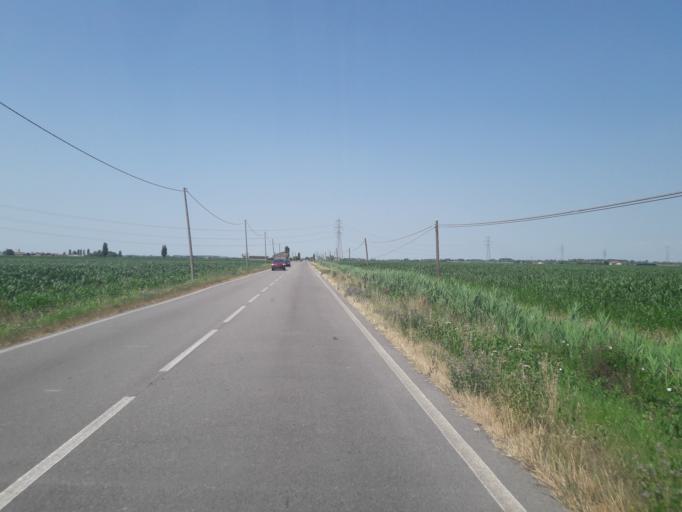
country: IT
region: Veneto
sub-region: Provincia di Rovigo
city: Papozze
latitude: 45.0050
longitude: 12.1793
